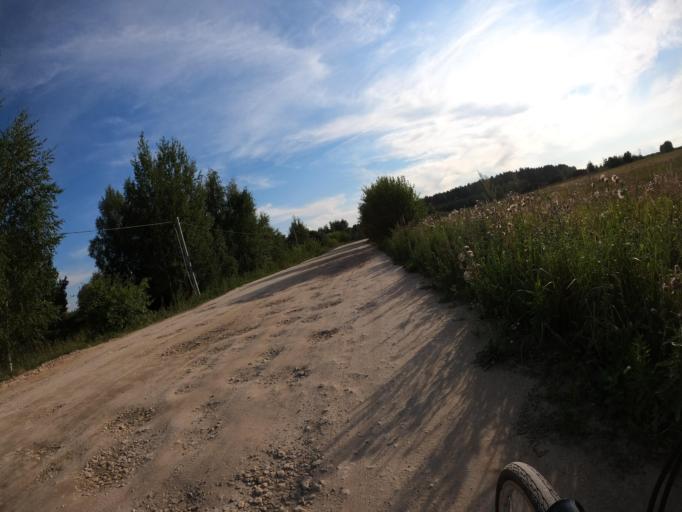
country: RU
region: Moskovskaya
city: Meshcherino
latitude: 55.1406
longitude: 38.4338
